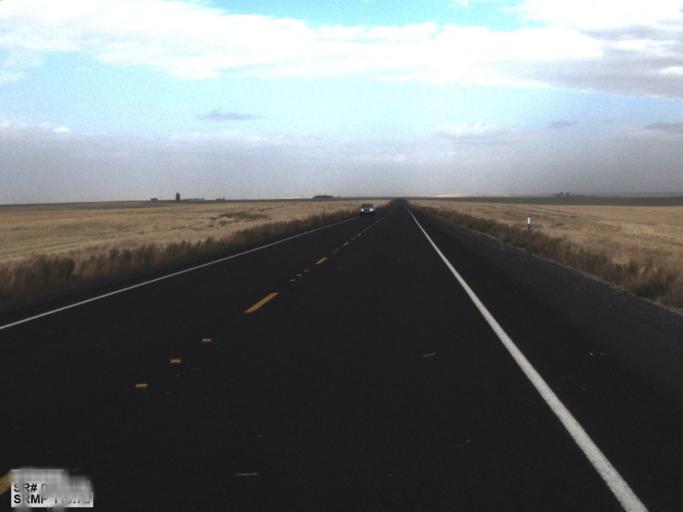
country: US
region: Washington
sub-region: Lincoln County
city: Davenport
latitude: 47.4444
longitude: -118.3220
